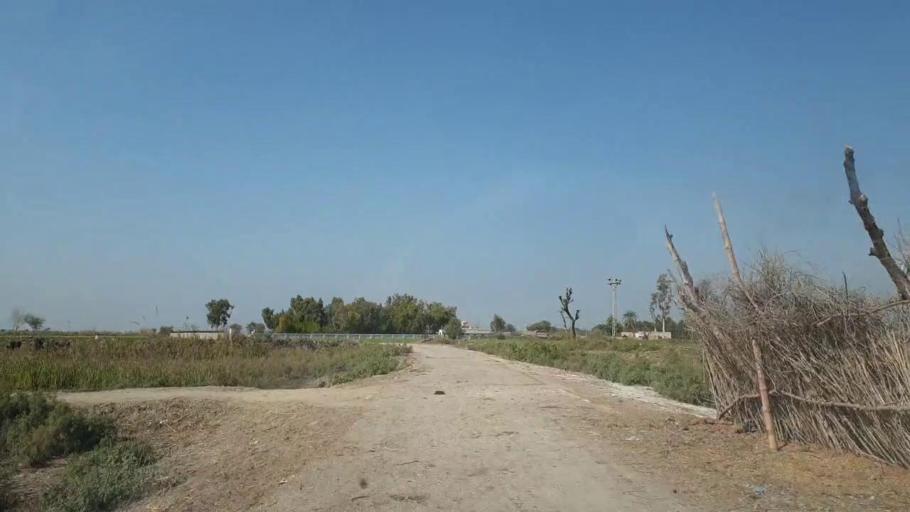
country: PK
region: Sindh
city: Mirpur Khas
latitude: 25.7174
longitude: 69.1303
